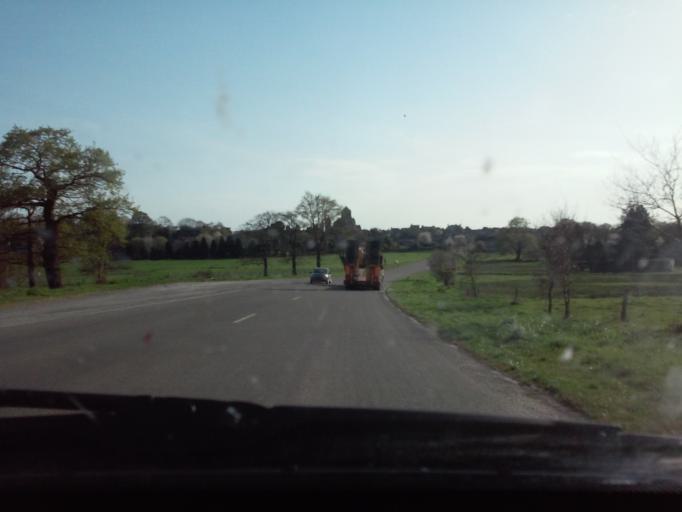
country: FR
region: Brittany
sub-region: Departement d'Ille-et-Vilaine
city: Saint-Aubin-du-Cormier
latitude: 48.2670
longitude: -1.3936
